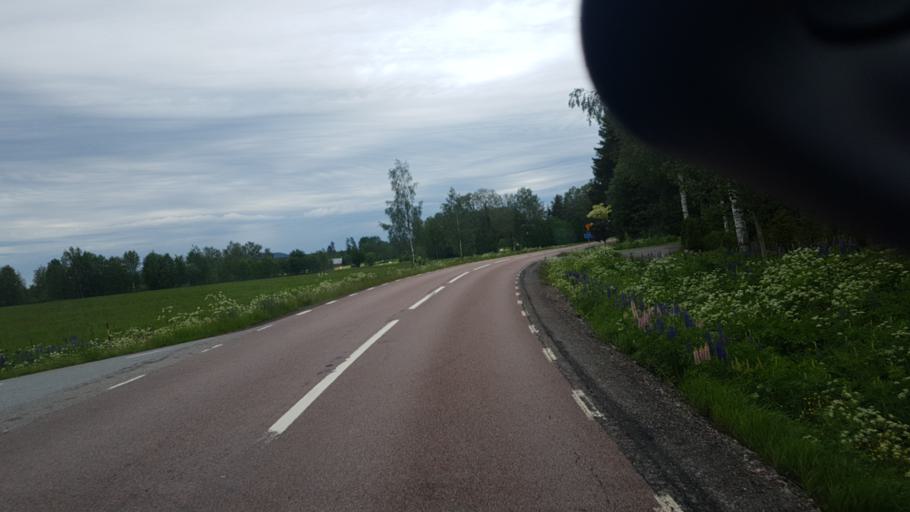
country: SE
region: Vaermland
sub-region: Eda Kommun
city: Amotfors
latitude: 59.7600
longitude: 12.2136
